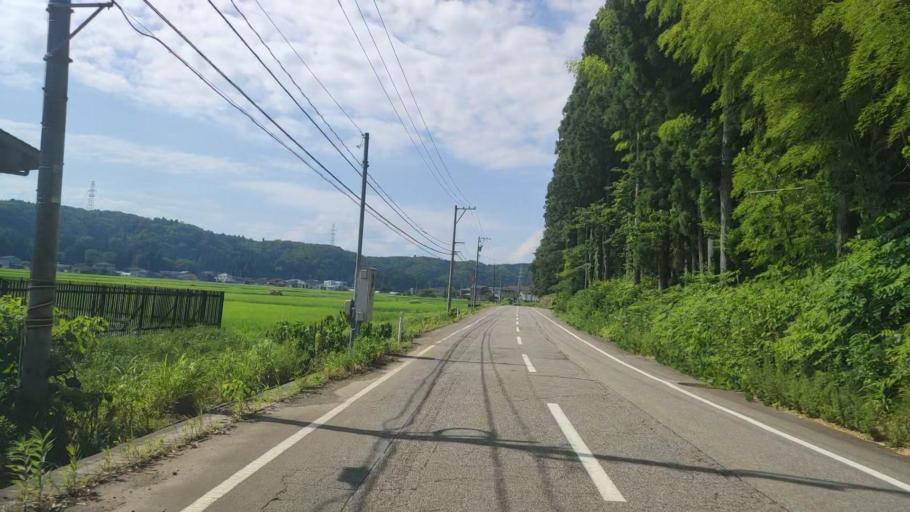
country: JP
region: Ishikawa
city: Komatsu
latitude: 36.3766
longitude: 136.4968
